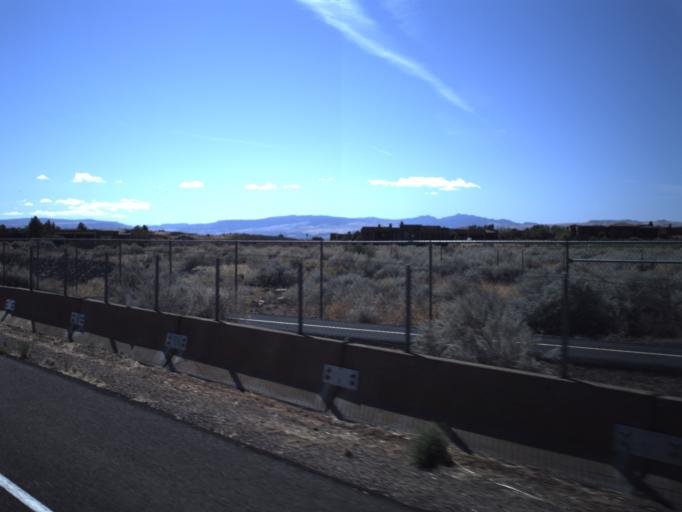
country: US
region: Utah
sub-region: Washington County
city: Ivins
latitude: 37.2014
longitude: -113.6257
